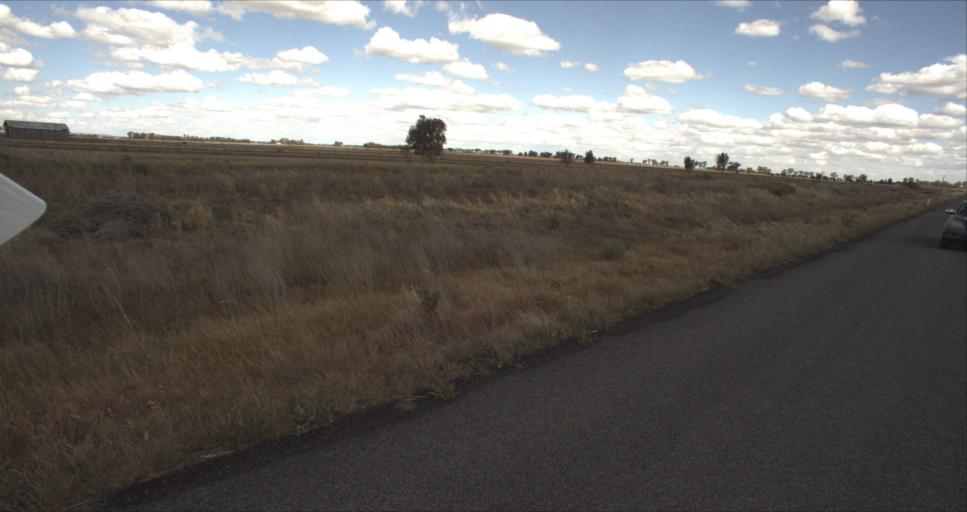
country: AU
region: New South Wales
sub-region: Leeton
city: Leeton
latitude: -34.4473
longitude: 146.2552
